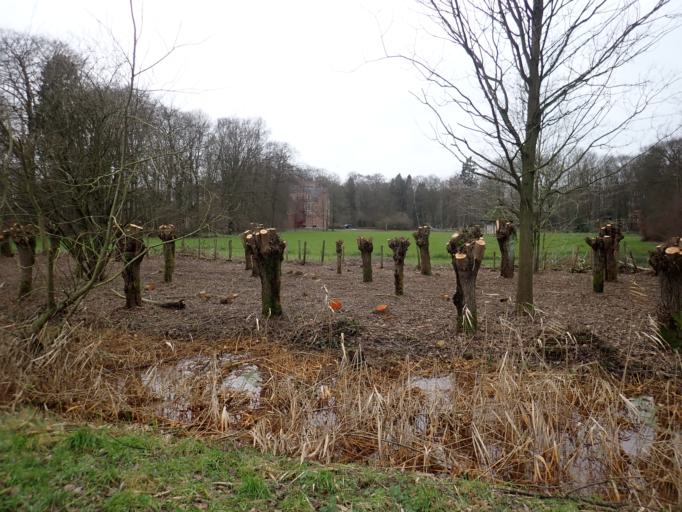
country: BE
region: Flanders
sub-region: Provincie Antwerpen
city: Zandhoven
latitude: 51.2497
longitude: 4.6317
